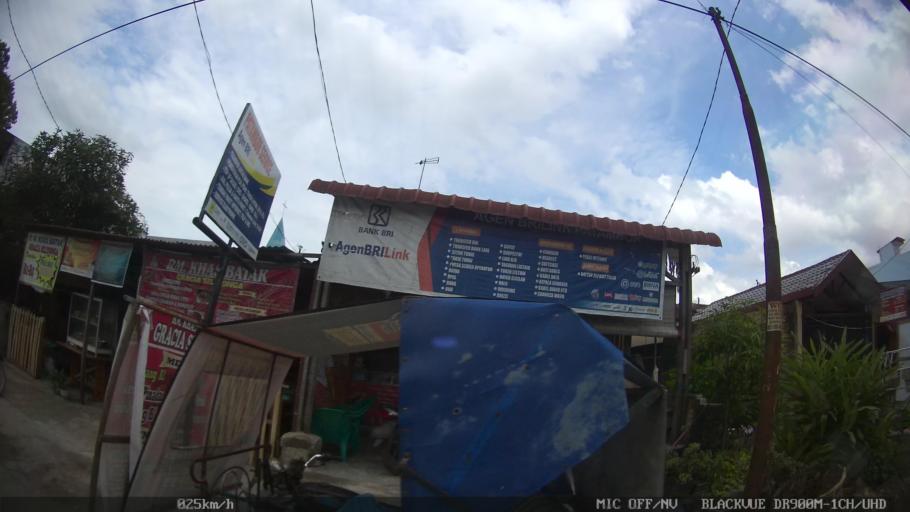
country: ID
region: North Sumatra
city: Sunggal
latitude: 3.6173
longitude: 98.6241
